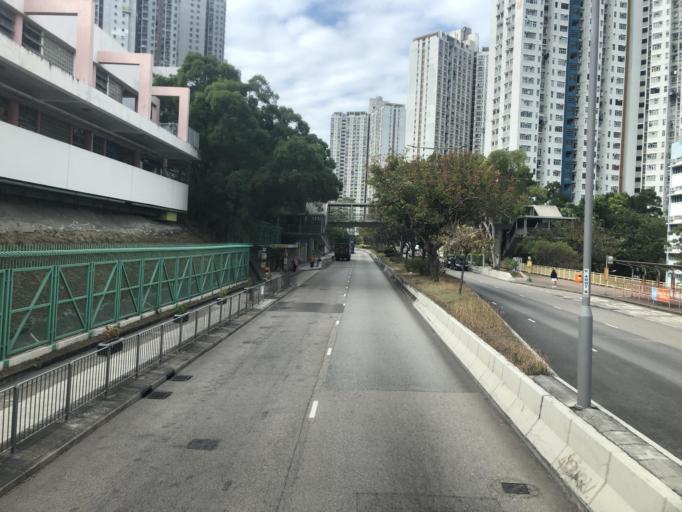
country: HK
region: Tsuen Wan
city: Tsuen Wan
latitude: 22.3488
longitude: 114.1037
